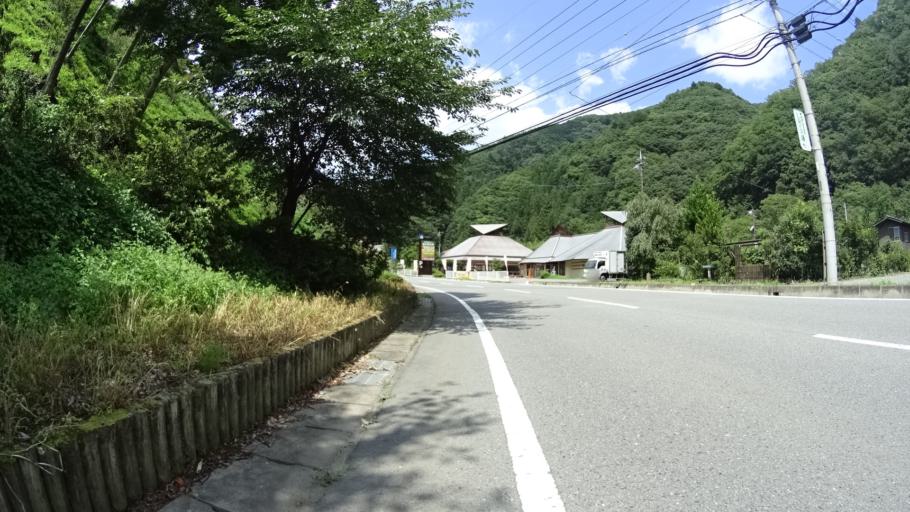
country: JP
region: Gunma
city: Tomioka
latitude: 36.0872
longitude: 138.7263
